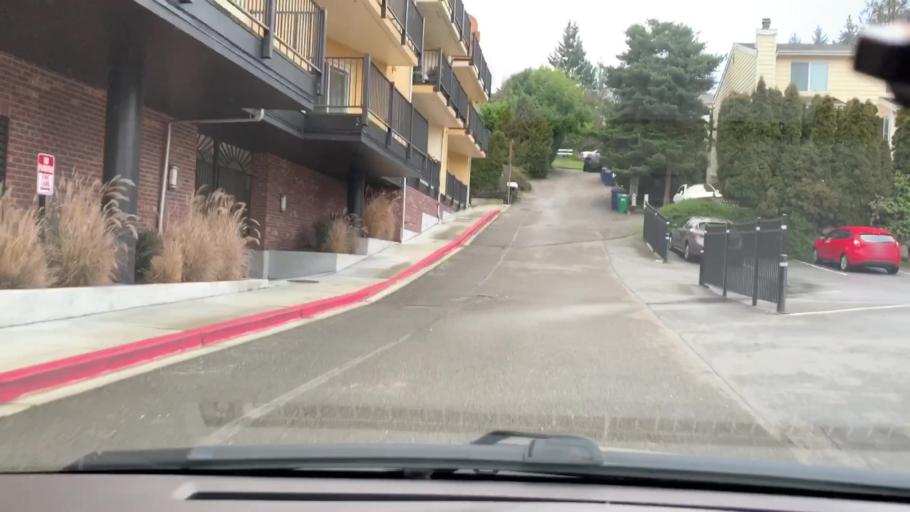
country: US
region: Washington
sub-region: King County
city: Kirkland
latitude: 47.7057
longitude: -122.2100
